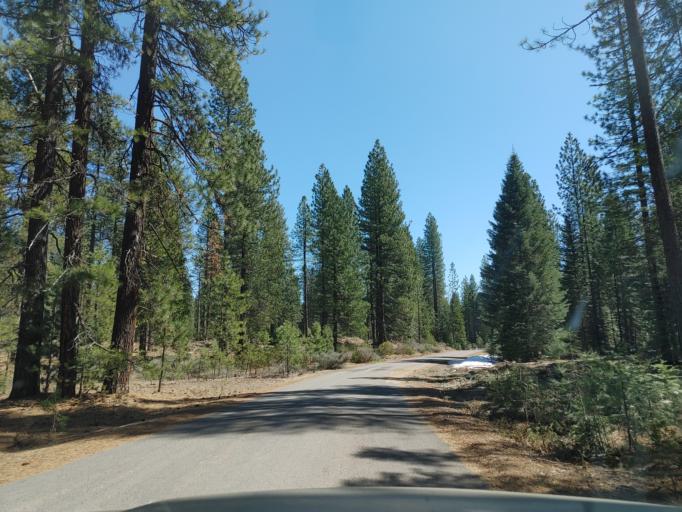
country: US
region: California
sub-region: Siskiyou County
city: McCloud
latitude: 41.2537
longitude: -121.9461
